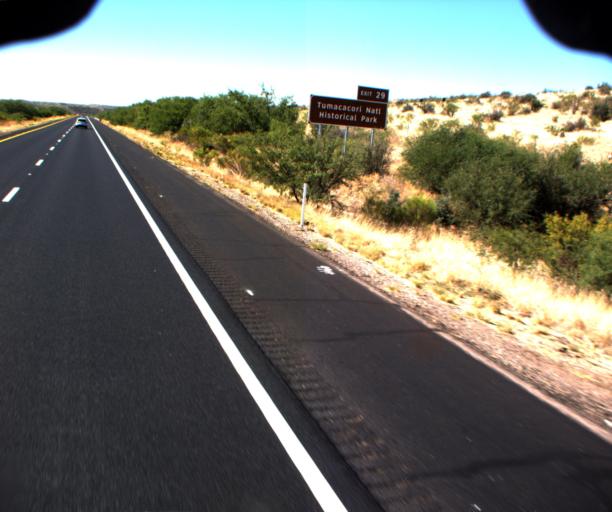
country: US
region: Arizona
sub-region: Santa Cruz County
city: Tubac
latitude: 31.5651
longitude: -111.0534
